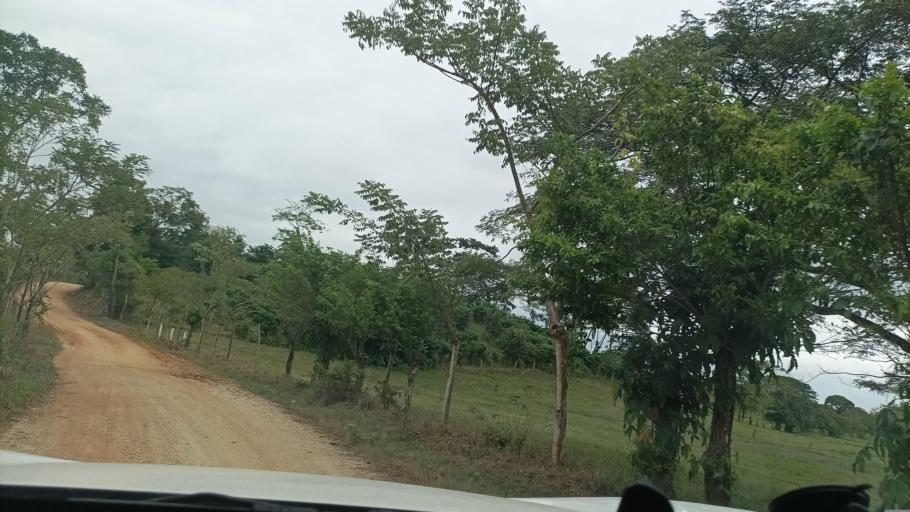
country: MX
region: Veracruz
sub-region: Uxpanapa
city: Poblado Cinco
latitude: 17.4993
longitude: -94.5647
